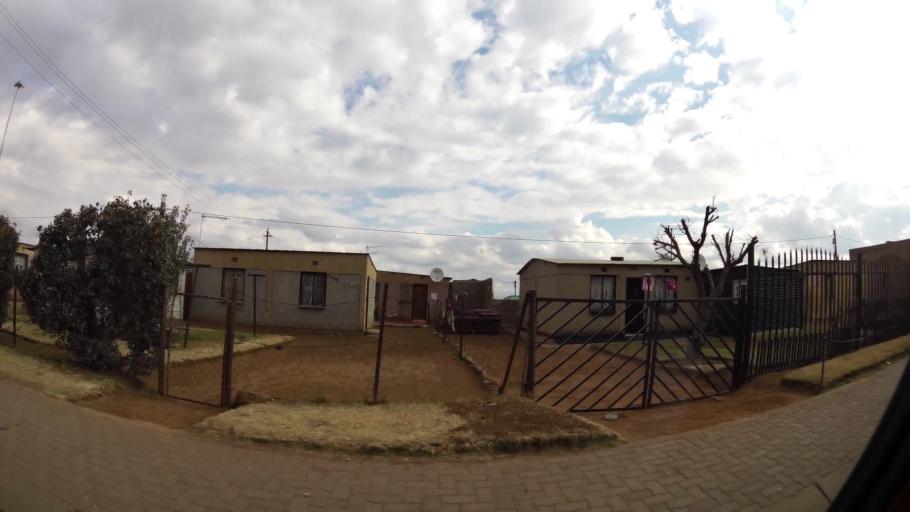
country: ZA
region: Gauteng
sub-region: Sedibeng District Municipality
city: Vanderbijlpark
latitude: -26.6999
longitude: 27.8023
